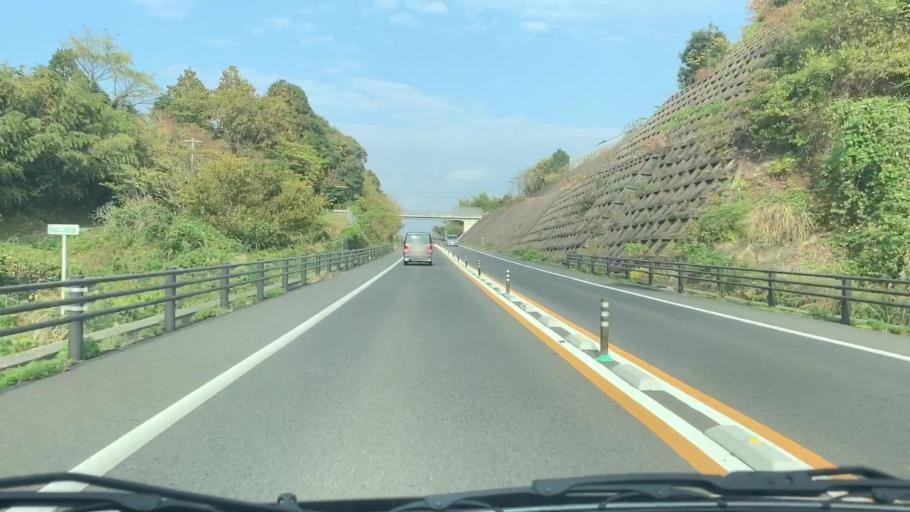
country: JP
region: Nagasaki
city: Sasebo
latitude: 33.0233
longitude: 129.7350
